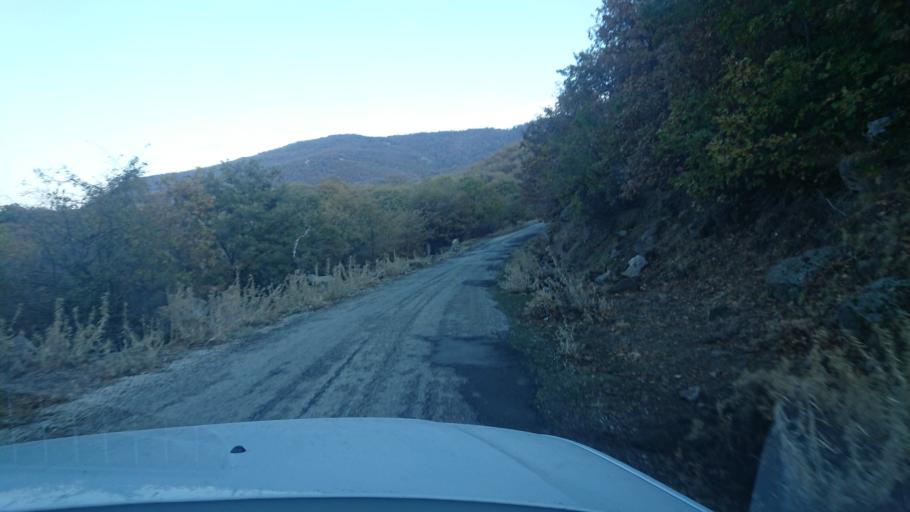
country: TR
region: Aksaray
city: Taspinar
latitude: 38.1658
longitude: 34.1991
